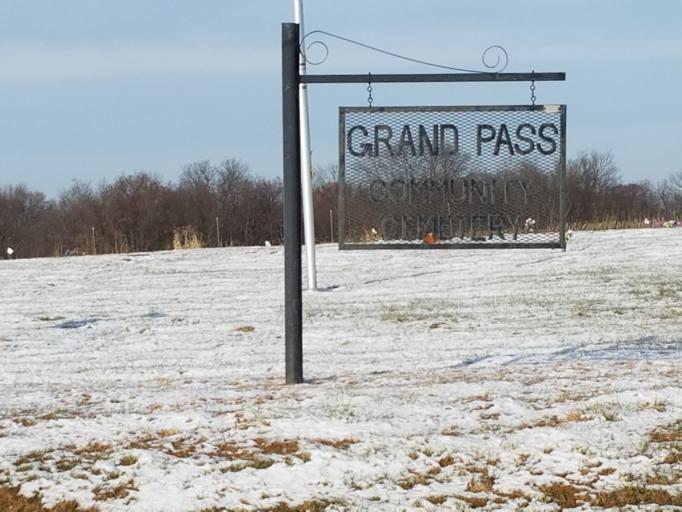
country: US
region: Missouri
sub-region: Carroll County
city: Carrollton
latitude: 39.2039
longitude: -93.4494
